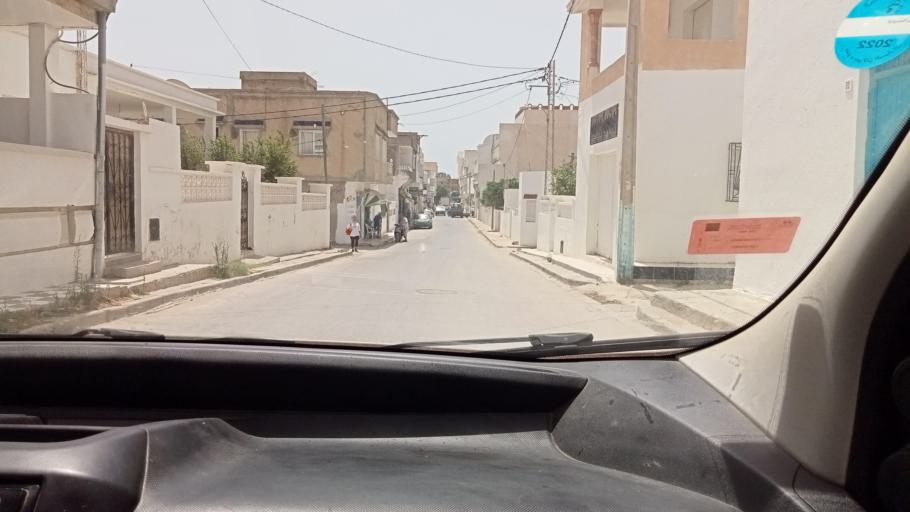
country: TN
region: Nabul
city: Qulaybiyah
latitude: 36.8510
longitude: 11.0871
